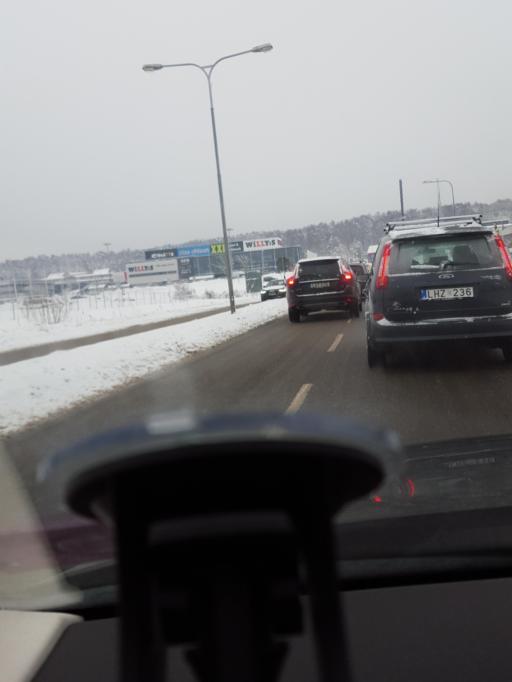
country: SE
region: Vaestra Goetaland
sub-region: Goteborg
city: Majorna
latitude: 57.6429
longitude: 11.9515
